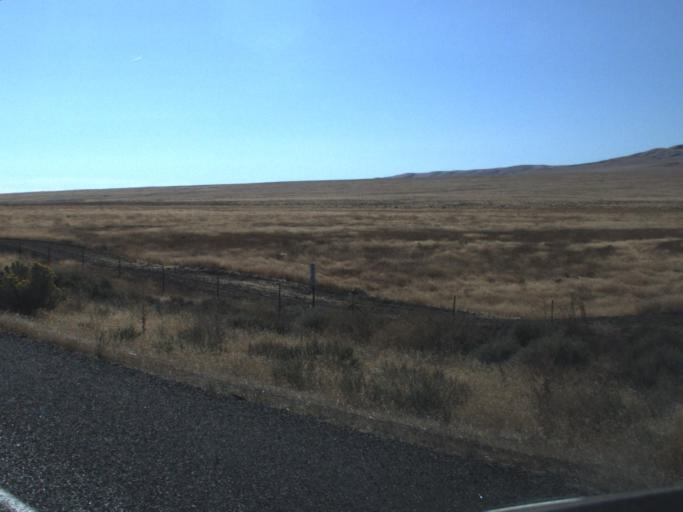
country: US
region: Washington
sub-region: Benton County
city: Benton City
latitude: 46.4776
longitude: -119.5639
